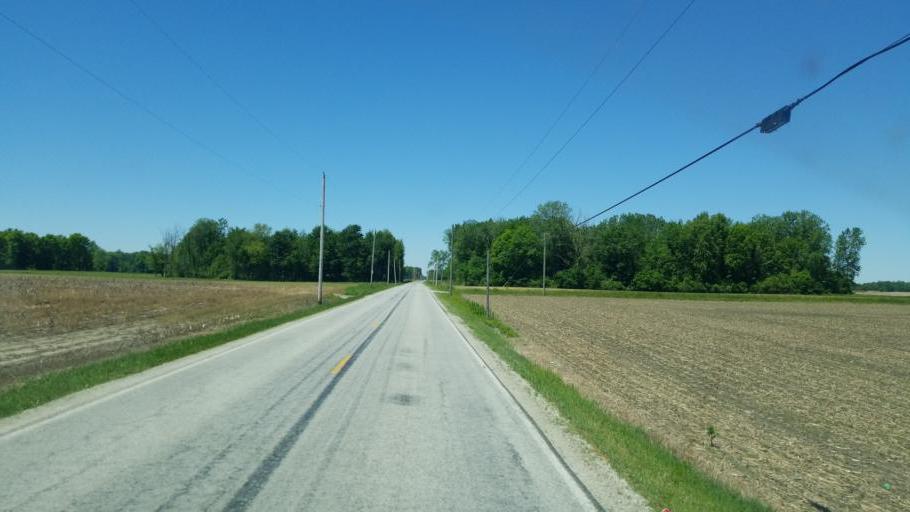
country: US
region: Ohio
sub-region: Shelby County
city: Fort Loramie
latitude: 40.3552
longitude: -84.3265
